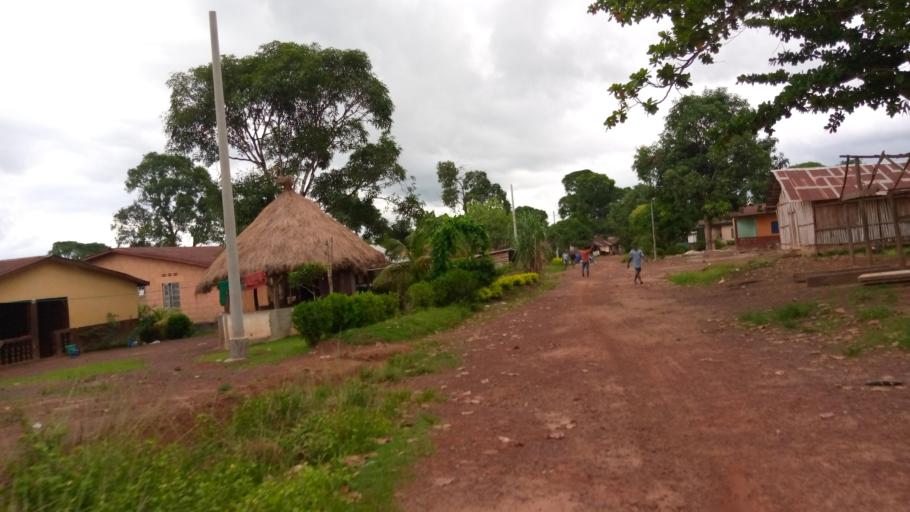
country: SL
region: Southern Province
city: Moyamba
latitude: 8.1637
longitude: -12.4402
